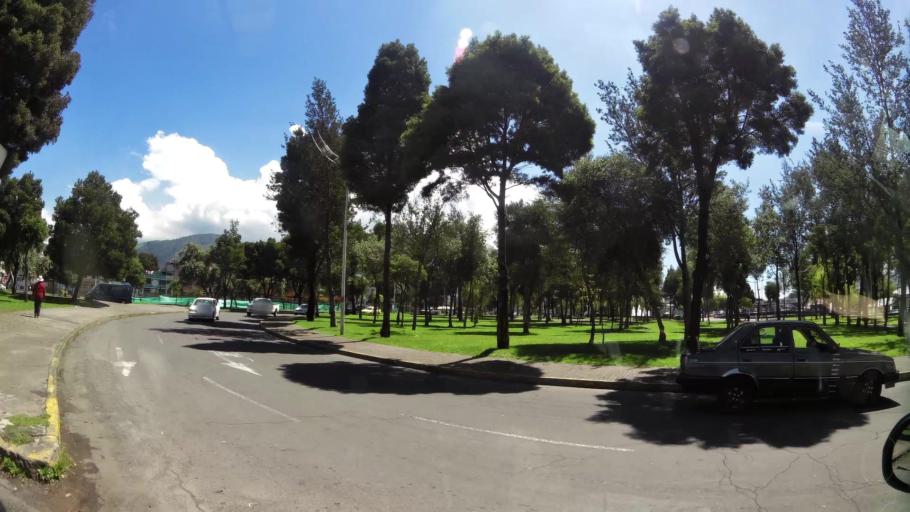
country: EC
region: Pichincha
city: Quito
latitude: -0.2736
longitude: -78.5376
